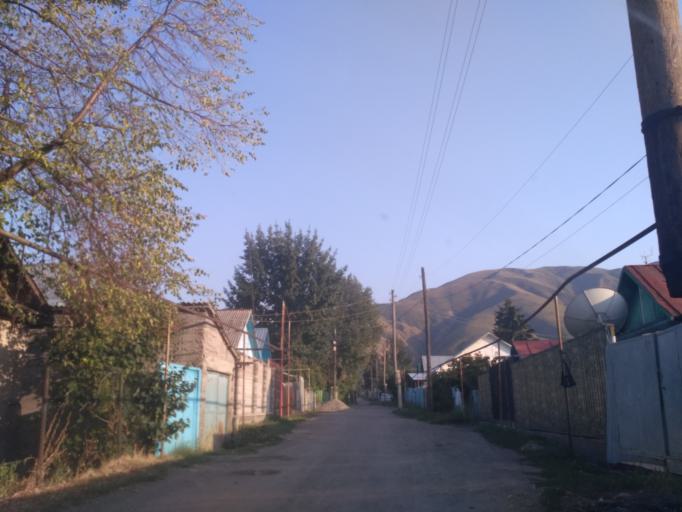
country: KZ
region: Almaty Oblysy
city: Burunday
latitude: 43.1623
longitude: 76.4058
